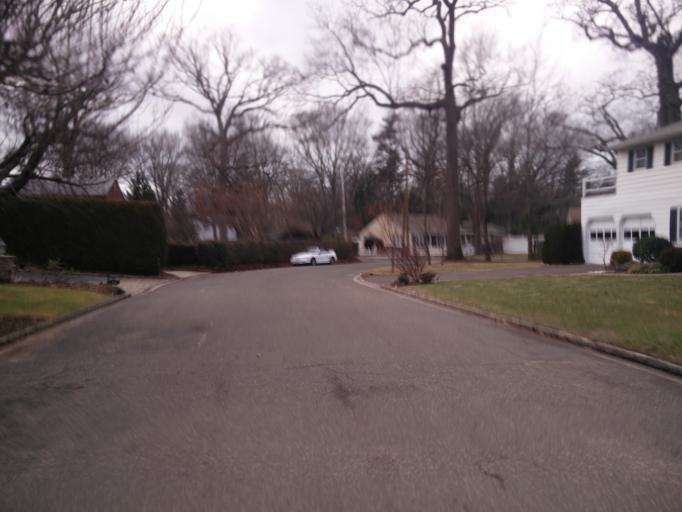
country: US
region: New York
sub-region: Nassau County
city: Glen Cove
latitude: 40.8774
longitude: -73.6290
